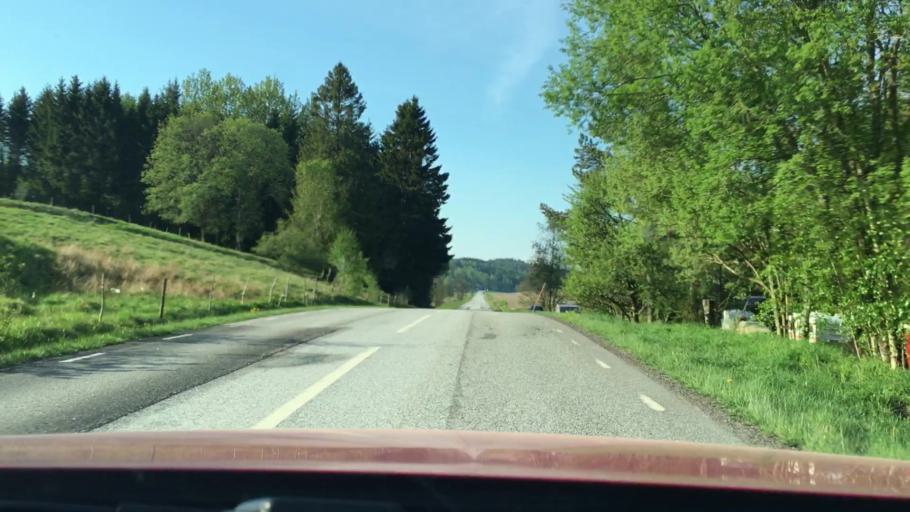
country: SE
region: Vaestra Goetaland
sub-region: Munkedals Kommun
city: Munkedal
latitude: 58.6148
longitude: 11.5587
